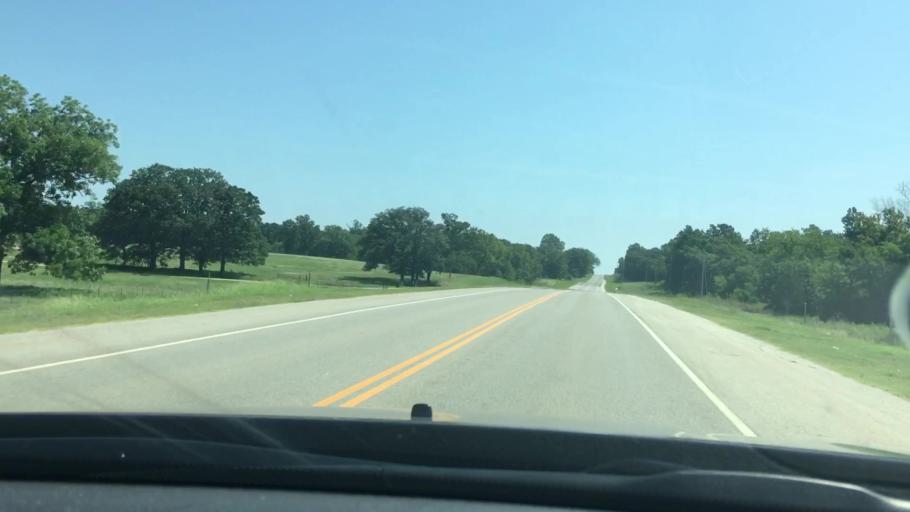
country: US
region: Oklahoma
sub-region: Johnston County
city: Tishomingo
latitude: 34.2746
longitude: -96.5439
